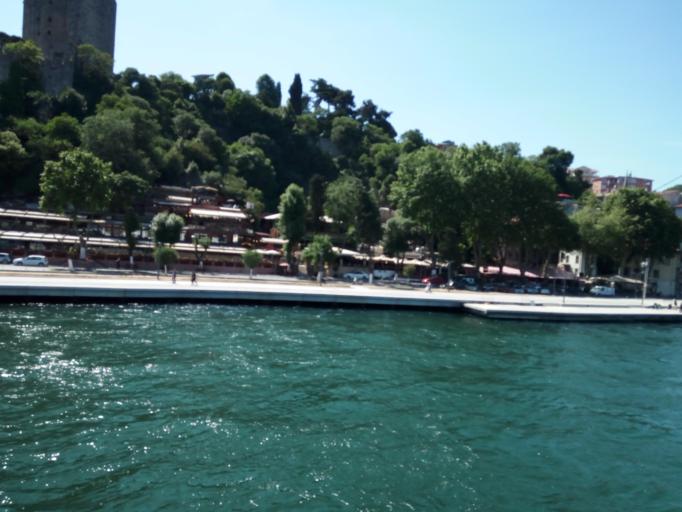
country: TR
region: Istanbul
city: UEskuedar
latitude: 41.0859
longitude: 29.0579
